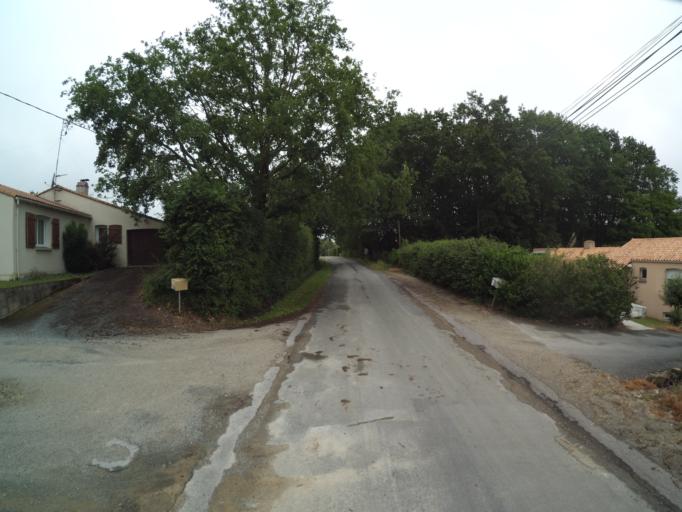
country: FR
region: Pays de la Loire
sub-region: Departement de la Vendee
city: La Roche-sur-Yon
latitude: 46.6346
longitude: -1.4285
